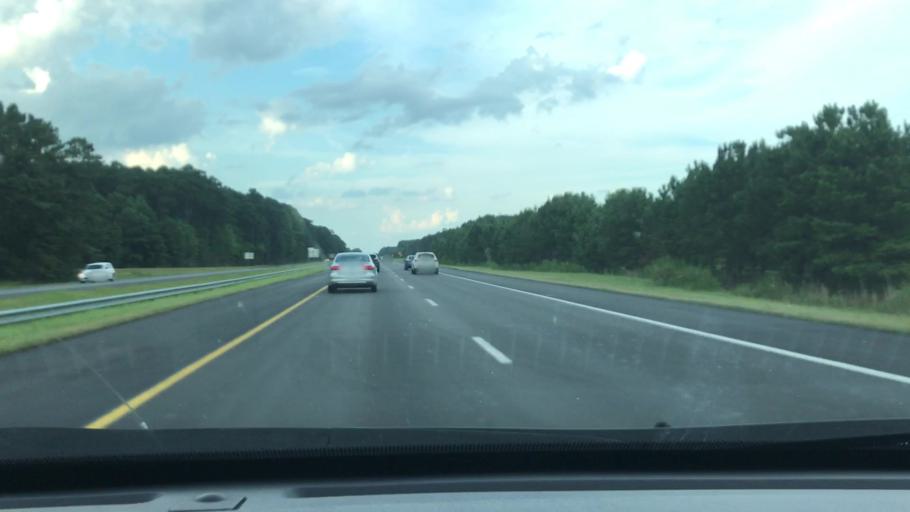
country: US
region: North Carolina
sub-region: Cumberland County
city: Eastover
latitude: 35.1244
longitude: -78.7528
